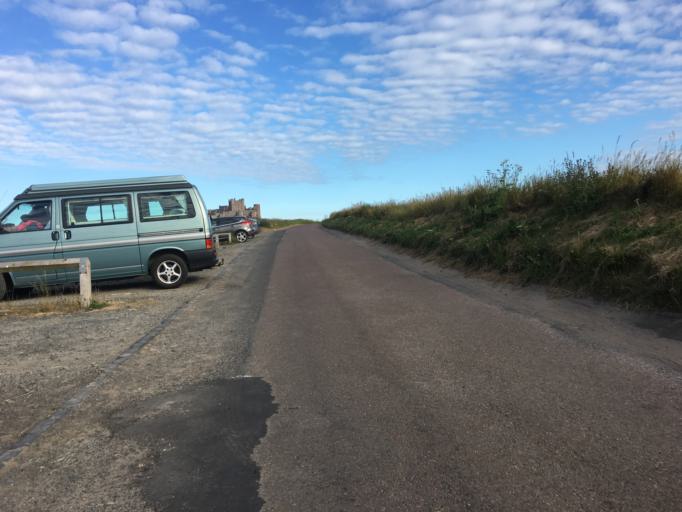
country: GB
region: England
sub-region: Northumberland
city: Bamburgh
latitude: 55.6150
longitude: -1.7222
